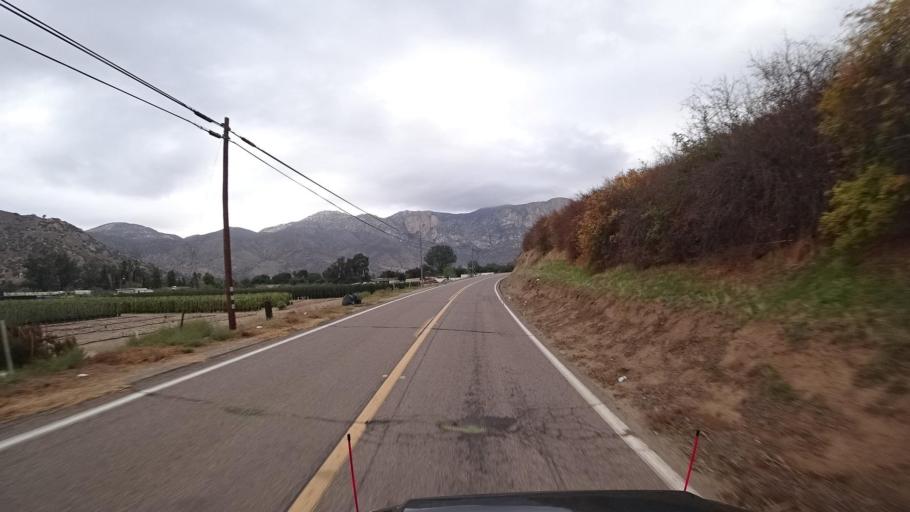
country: US
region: California
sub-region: San Diego County
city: Harbison Canyon
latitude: 32.8818
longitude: -116.8580
